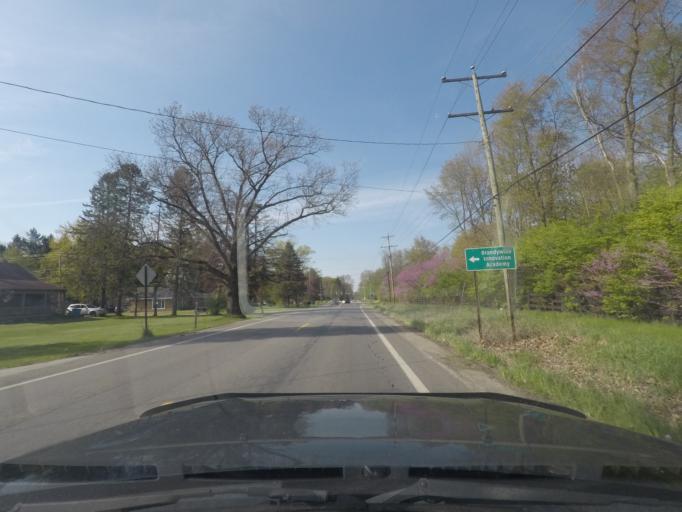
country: US
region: Michigan
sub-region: Berrien County
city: Niles
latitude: 41.7993
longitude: -86.2545
